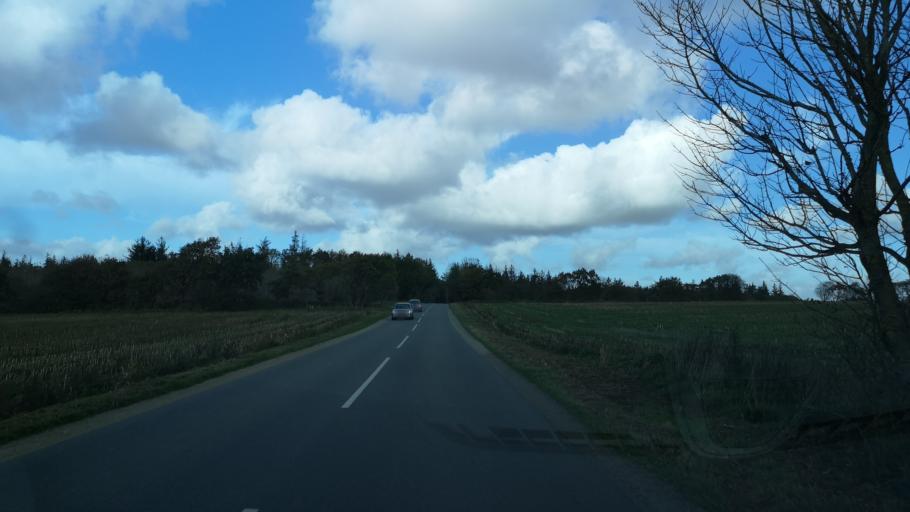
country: DK
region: South Denmark
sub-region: Varde Kommune
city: Oksbol
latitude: 55.7379
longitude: 8.2517
